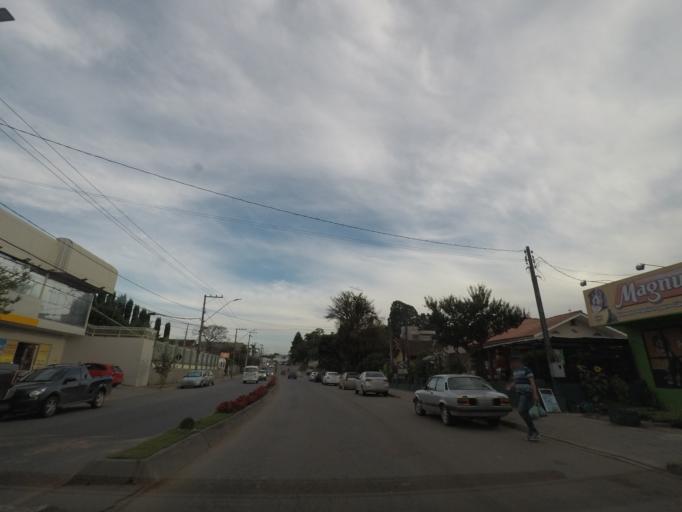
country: BR
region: Parana
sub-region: Colombo
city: Colombo
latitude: -25.2942
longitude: -49.2238
